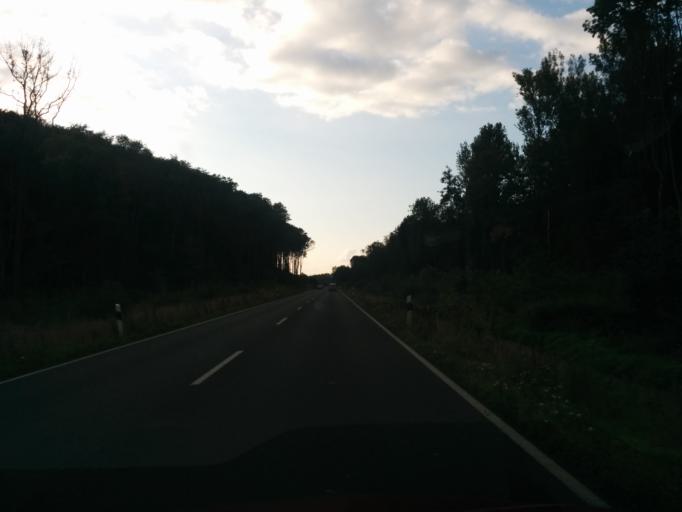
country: DE
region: Lower Saxony
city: Northeim
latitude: 51.7035
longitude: 10.0392
